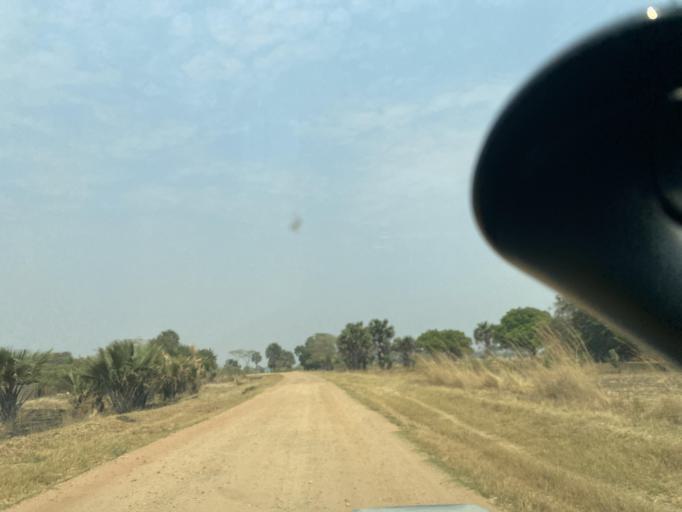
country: ZM
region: Lusaka
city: Kafue
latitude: -15.6480
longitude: 28.0349
